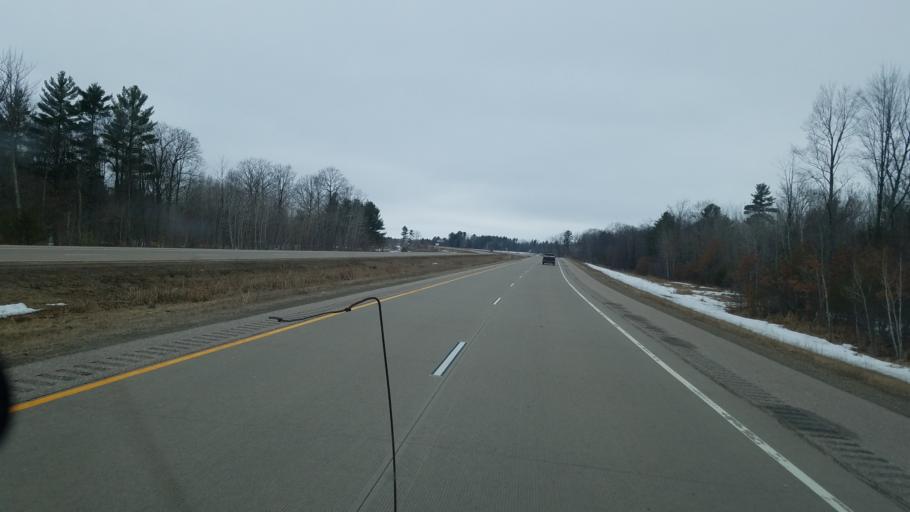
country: US
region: Wisconsin
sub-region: Portage County
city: Stevens Point
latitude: 44.5996
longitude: -89.6707
